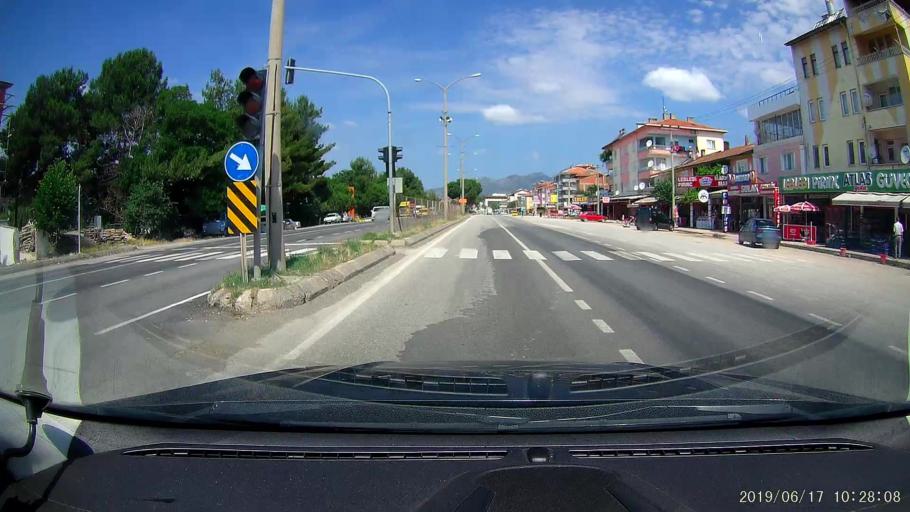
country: TR
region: Corum
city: Osmancik
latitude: 40.9766
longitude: 34.8115
